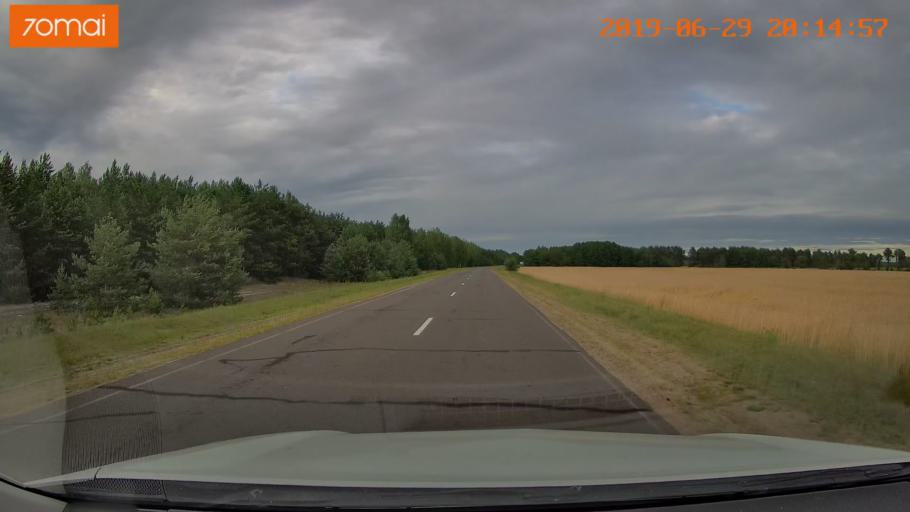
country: BY
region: Brest
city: Lahishyn
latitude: 52.3706
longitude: 26.1663
